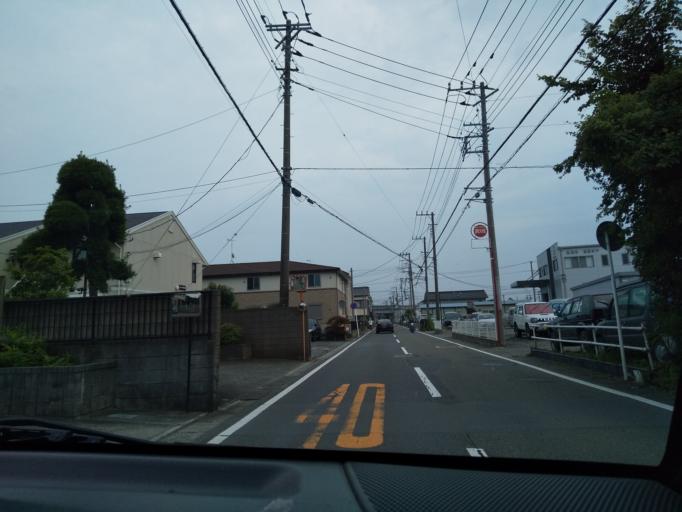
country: JP
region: Kanagawa
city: Atsugi
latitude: 35.3984
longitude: 139.3851
